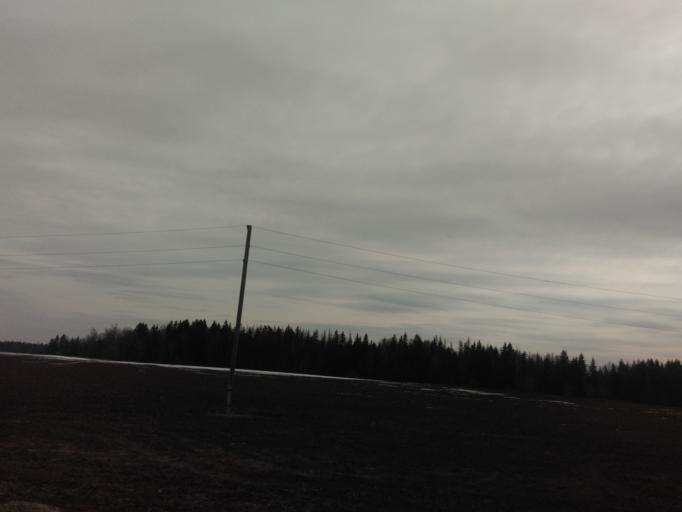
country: RU
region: Moskovskaya
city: Kolyubakino
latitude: 55.6903
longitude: 36.5690
